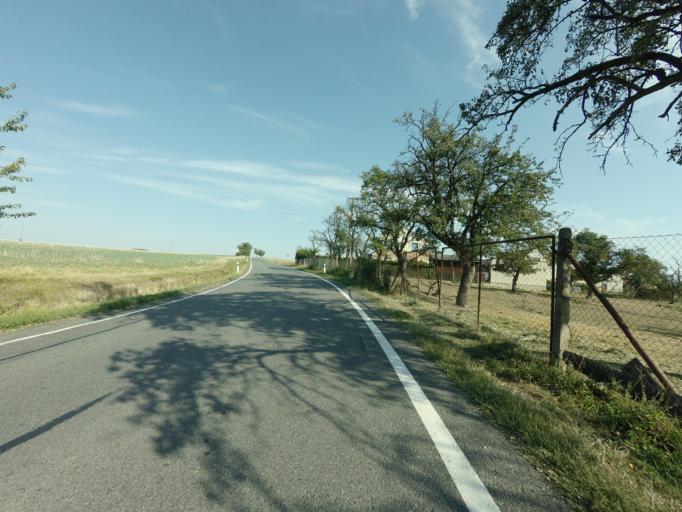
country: CZ
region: Jihocesky
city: Bernartice
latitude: 49.3063
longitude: 14.3801
